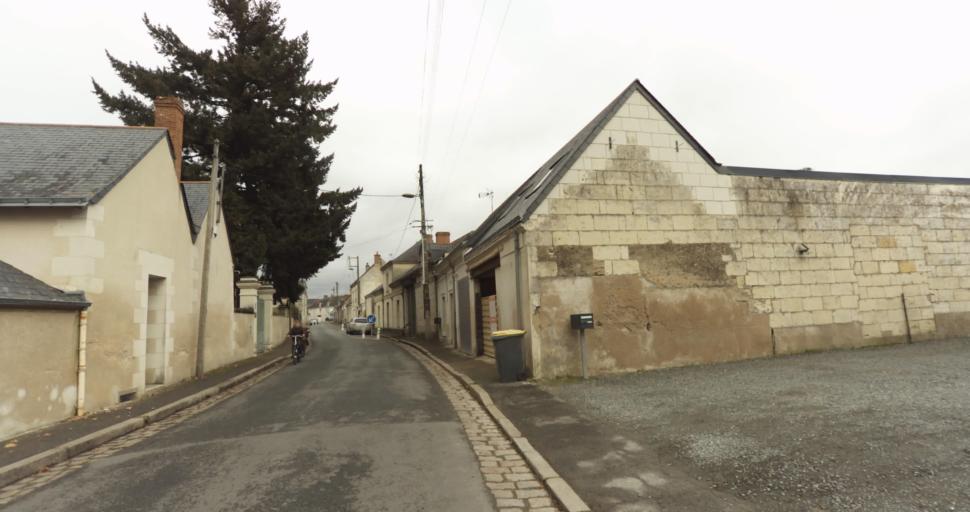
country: FR
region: Pays de la Loire
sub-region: Departement de Maine-et-Loire
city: Jumelles
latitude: 47.3757
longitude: -0.1217
